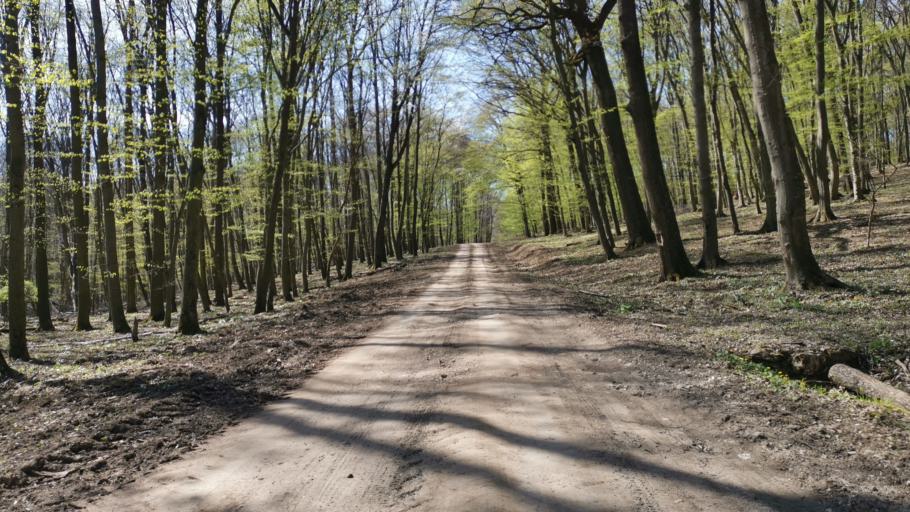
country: SK
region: Trnavsky
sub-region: Okres Skalica
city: Holic
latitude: 48.7374
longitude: 17.2362
